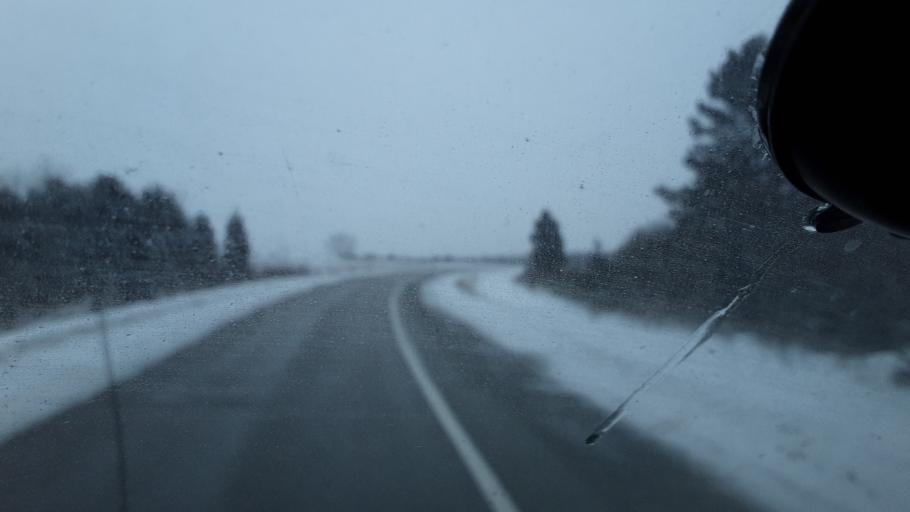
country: US
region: Michigan
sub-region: Ingham County
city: Holt
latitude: 42.6732
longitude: -84.4963
